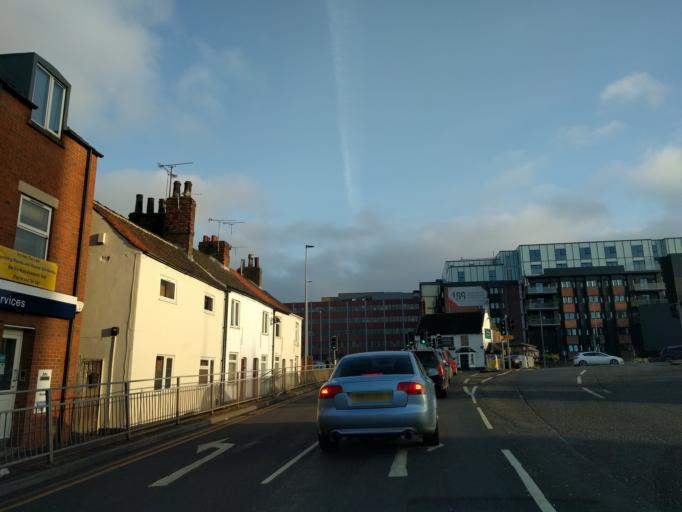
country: GB
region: England
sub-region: Lincolnshire
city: Lincoln
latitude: 53.2309
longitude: -0.5489
